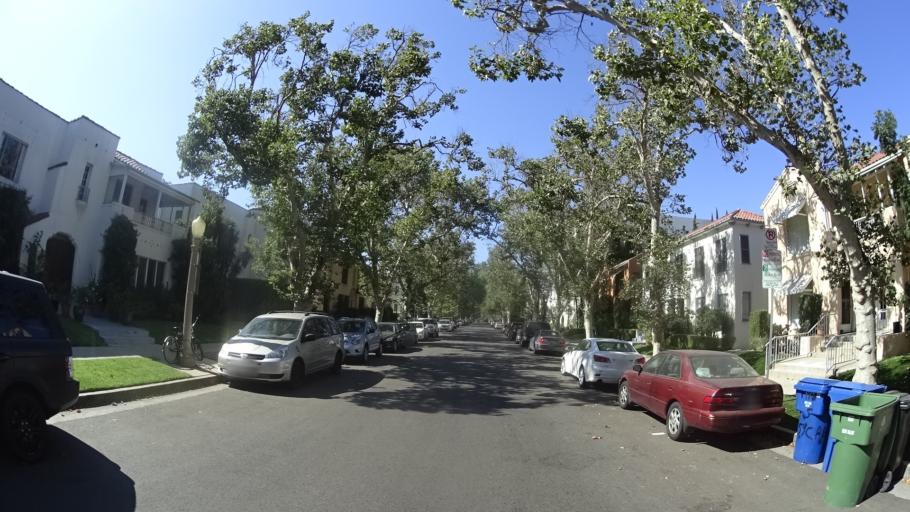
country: US
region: California
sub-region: Los Angeles County
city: West Hollywood
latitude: 34.0714
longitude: -118.3429
